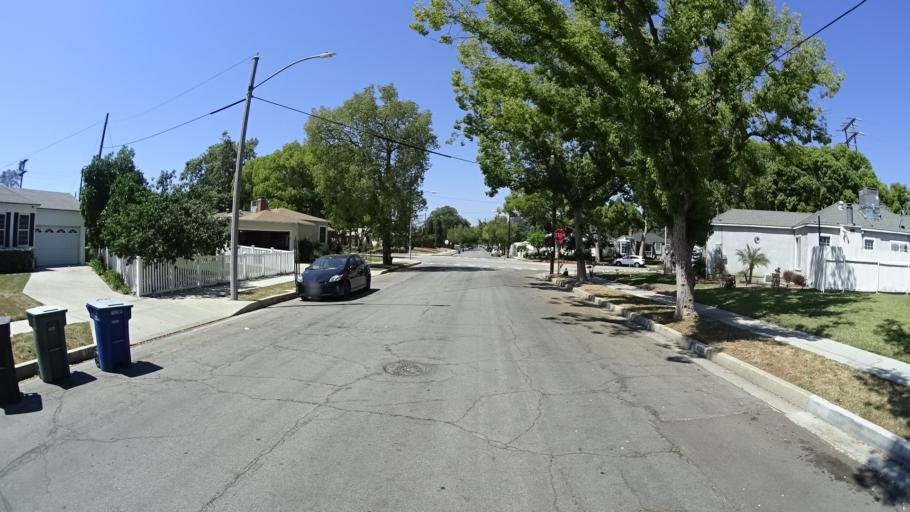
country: US
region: California
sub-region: Los Angeles County
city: North Hollywood
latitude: 34.1779
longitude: -118.3556
